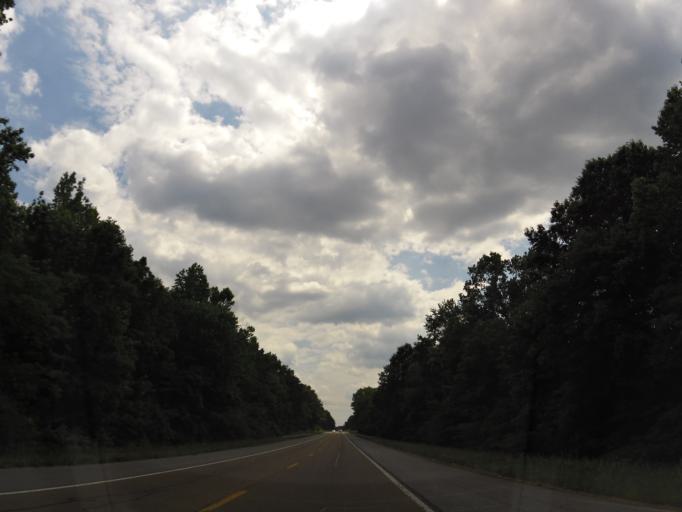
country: US
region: Tennessee
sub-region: Sequatchie County
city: Dunlap
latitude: 35.3095
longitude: -85.4372
